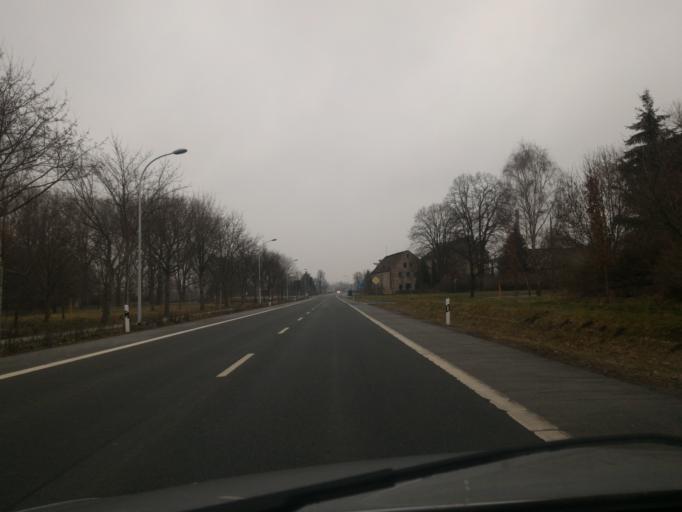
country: DE
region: Saxony
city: Zittau
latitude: 50.8968
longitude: 14.8308
